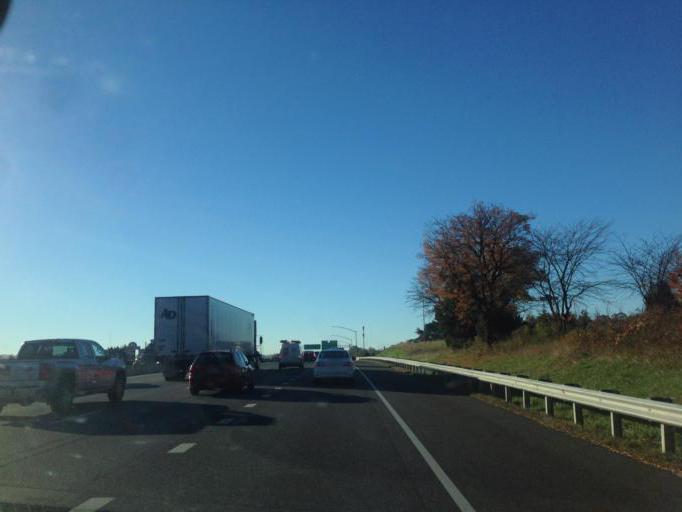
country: US
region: Maryland
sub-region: Baltimore County
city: Woodlawn
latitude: 39.3143
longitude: -76.7449
